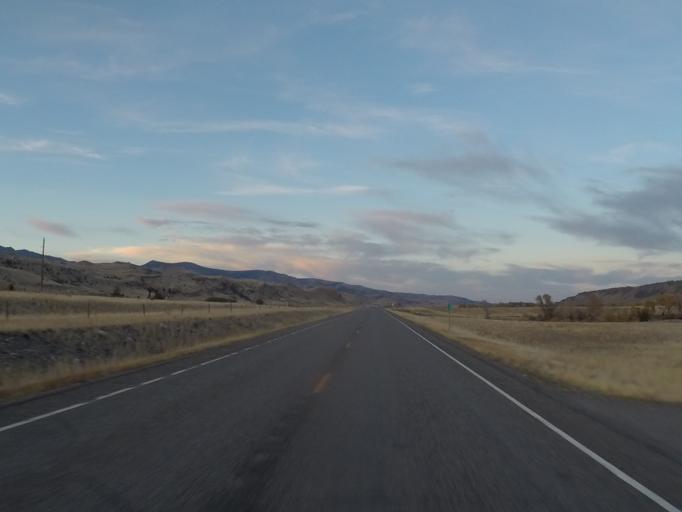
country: US
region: Montana
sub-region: Gallatin County
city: Bozeman
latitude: 45.2618
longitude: -110.8651
